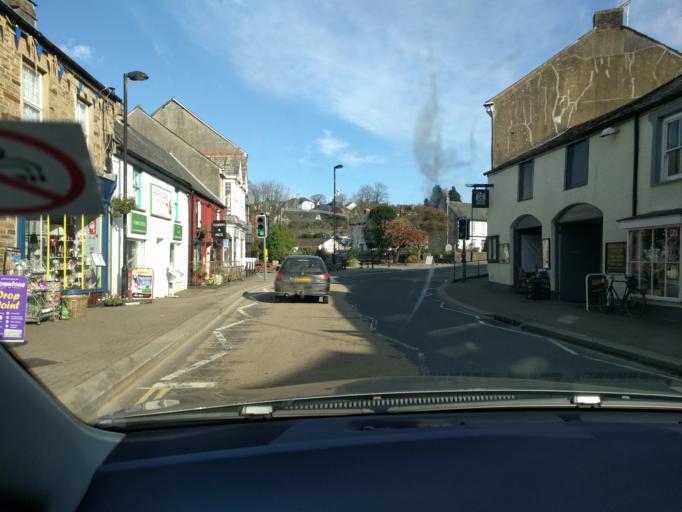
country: GB
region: England
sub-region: Cornwall
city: Camelford
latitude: 50.6230
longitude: -4.6788
